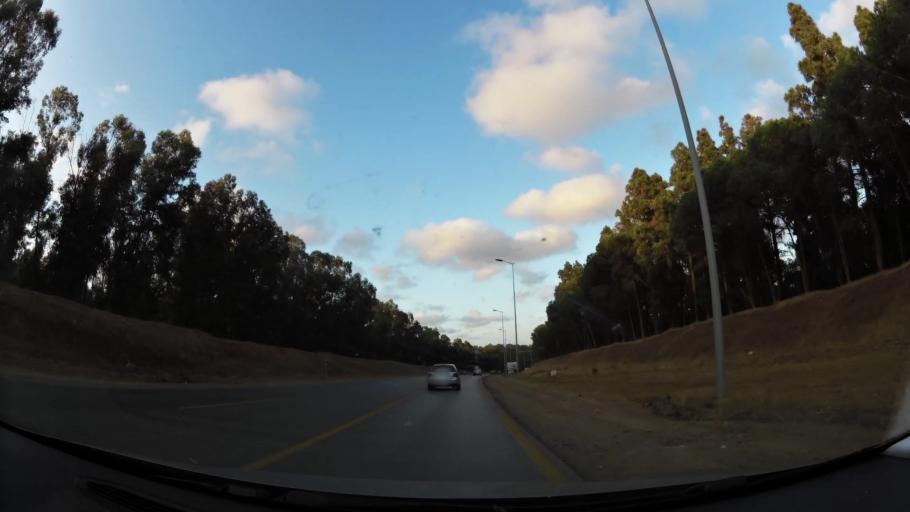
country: MA
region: Gharb-Chrarda-Beni Hssen
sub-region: Kenitra Province
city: Kenitra
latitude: 34.2467
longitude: -6.6198
